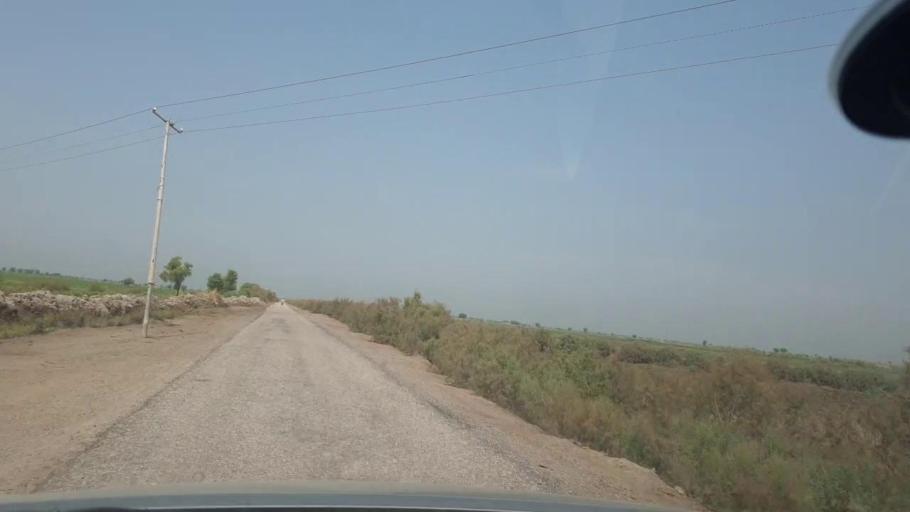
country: PK
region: Balochistan
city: Mehrabpur
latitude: 28.0583
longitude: 68.0737
